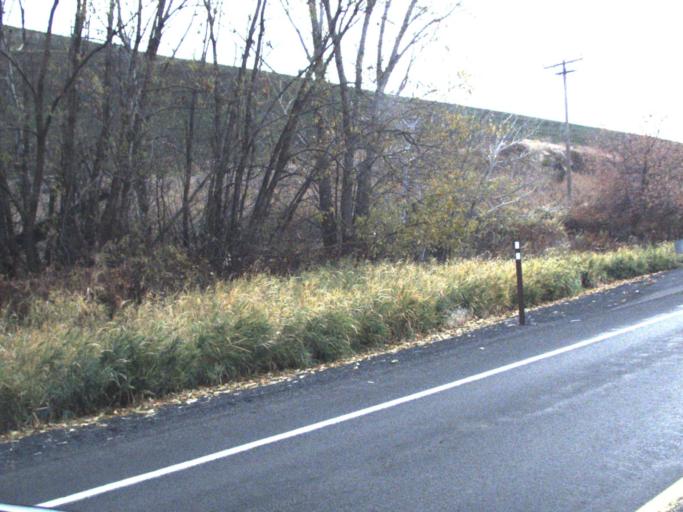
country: US
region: Washington
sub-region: Whitman County
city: Colfax
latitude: 46.8449
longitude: -117.4872
